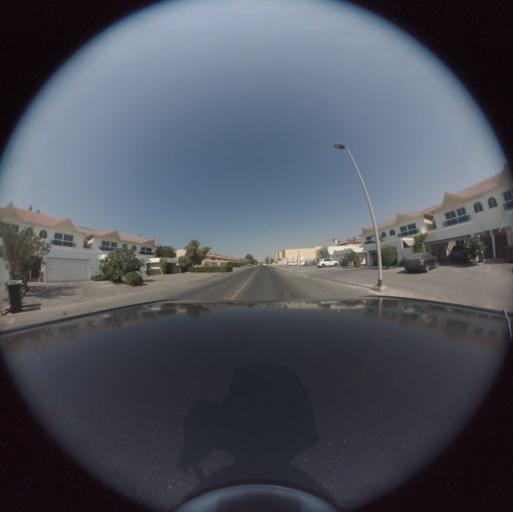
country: AE
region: Dubai
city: Dubai
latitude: 25.1794
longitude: 55.2386
